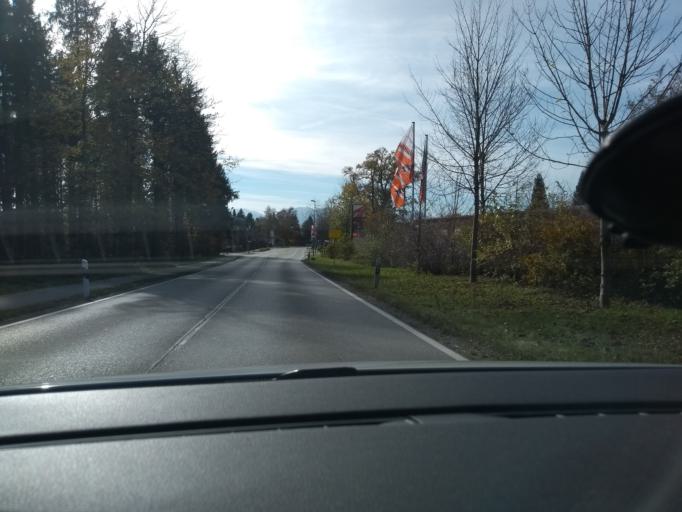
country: DE
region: Bavaria
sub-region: Upper Bavaria
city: Stephanskirchen
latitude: 47.8649
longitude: 12.1664
